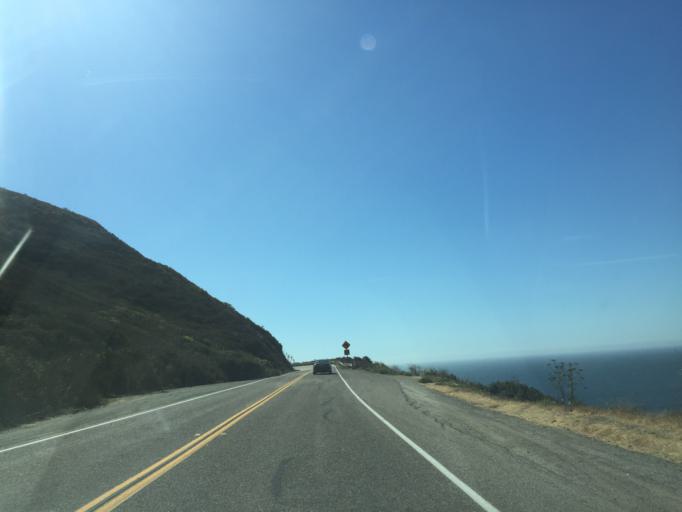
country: US
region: California
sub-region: Monterey County
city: Greenfield
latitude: 36.0510
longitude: -121.5881
